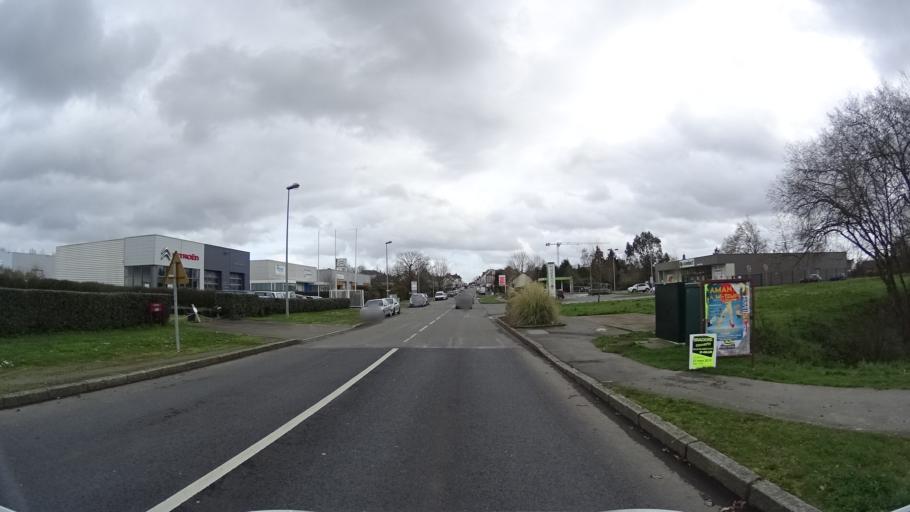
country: FR
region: Brittany
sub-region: Departement d'Ille-et-Vilaine
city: Saint-Gilles
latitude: 48.1566
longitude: -1.8336
